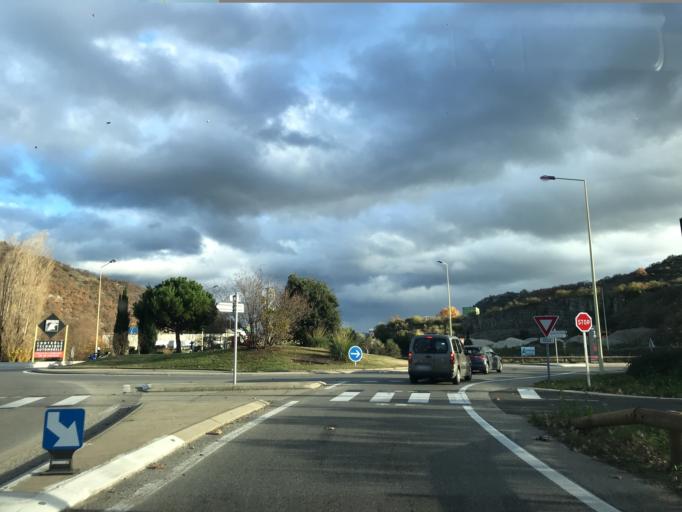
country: FR
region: Rhone-Alpes
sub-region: Departement de l'Ardeche
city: Alissas
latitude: 44.7163
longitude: 4.6114
